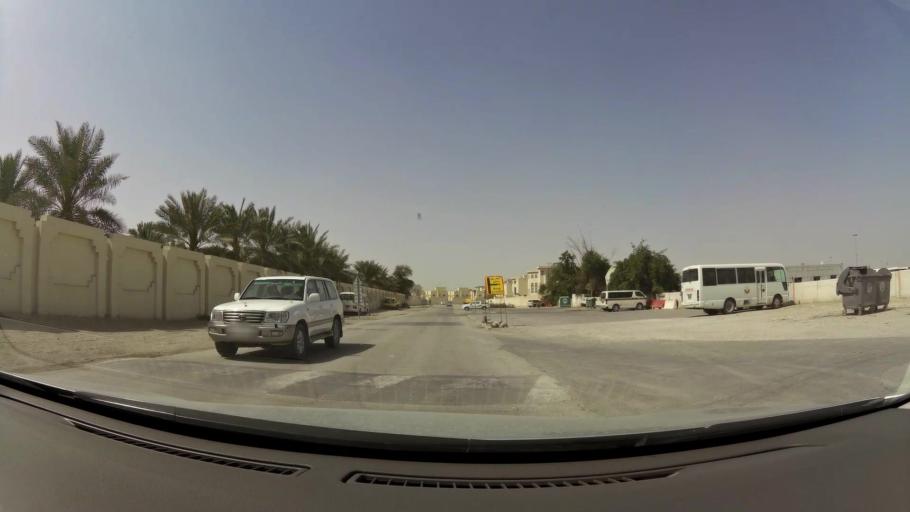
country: QA
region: Baladiyat Umm Salal
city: Umm Salal Muhammad
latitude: 25.3648
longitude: 51.4438
